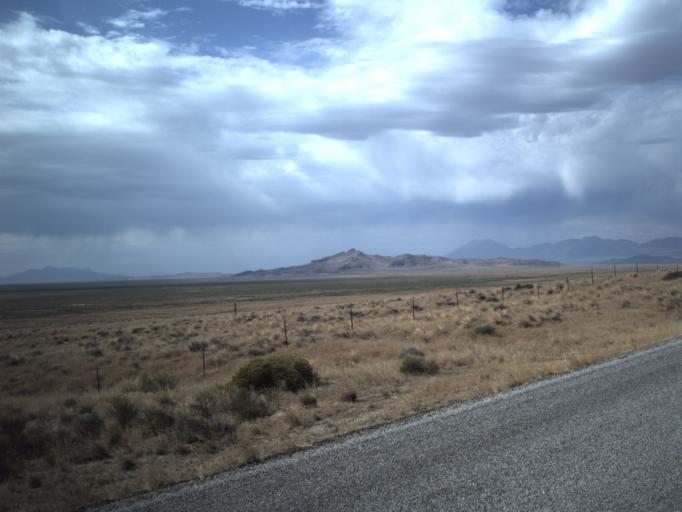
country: US
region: Utah
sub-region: Tooele County
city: Wendover
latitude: 41.4432
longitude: -113.6908
